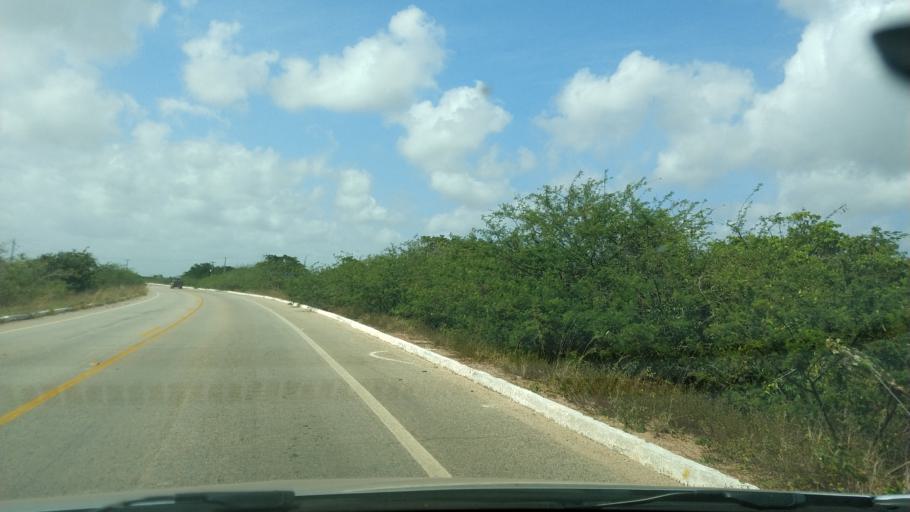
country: BR
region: Rio Grande do Norte
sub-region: Touros
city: Touros
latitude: -5.1811
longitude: -35.5113
